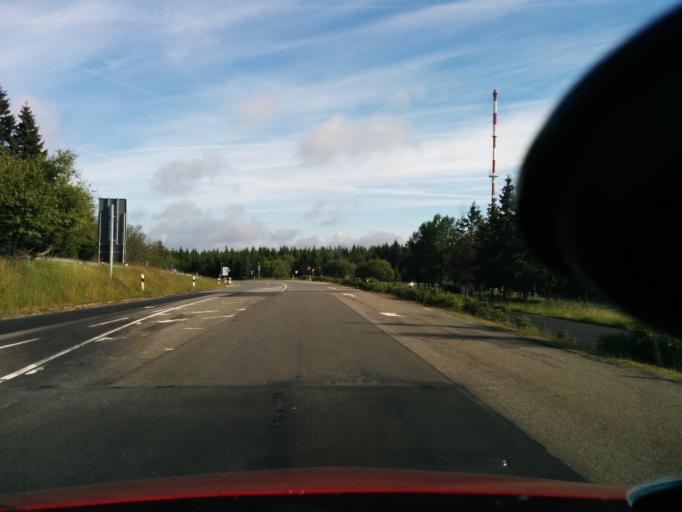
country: DE
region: Lower Saxony
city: Bad Harzburg
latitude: 51.8042
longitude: 10.5355
